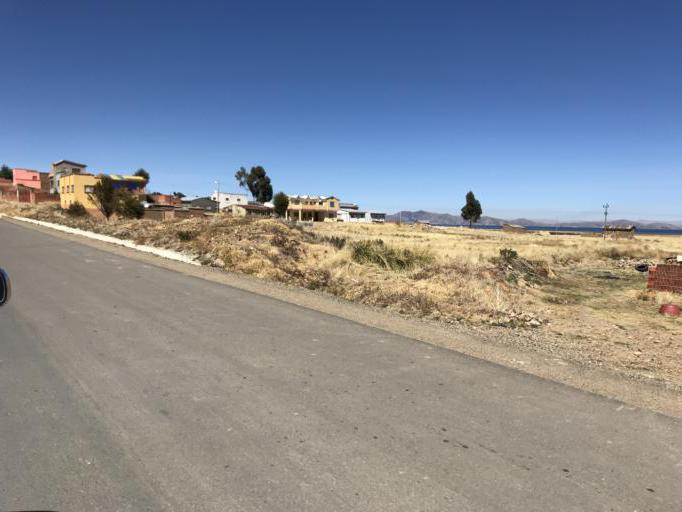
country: BO
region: La Paz
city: Huatajata
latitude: -16.1932
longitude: -68.7302
